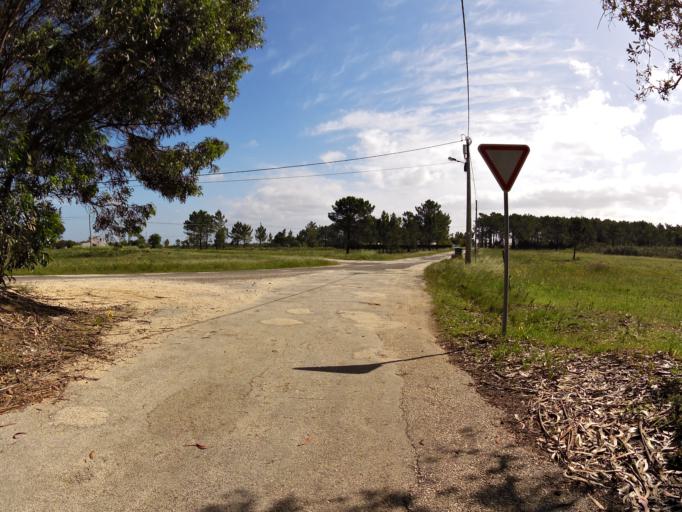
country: PT
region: Faro
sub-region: Aljezur
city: Aljezur
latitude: 37.3390
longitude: -8.8072
